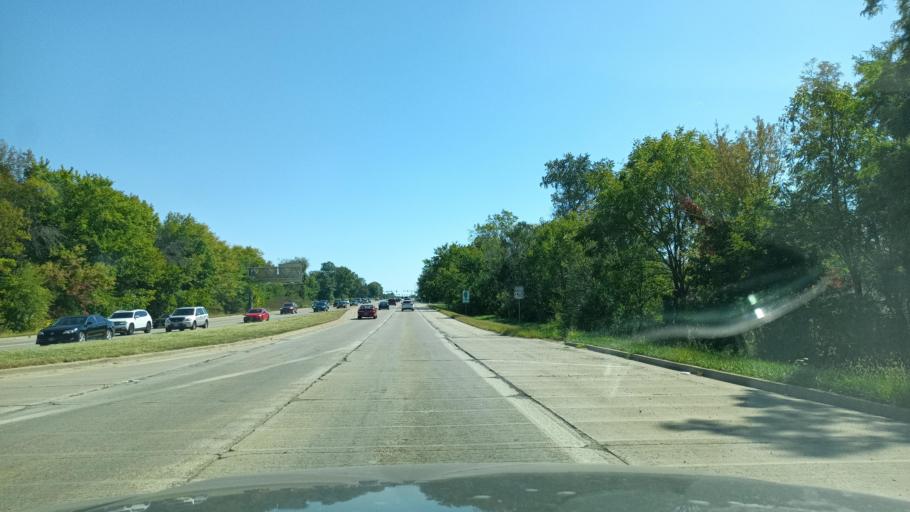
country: US
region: Illinois
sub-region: Peoria County
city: Dunlap
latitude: 40.7742
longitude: -89.6674
